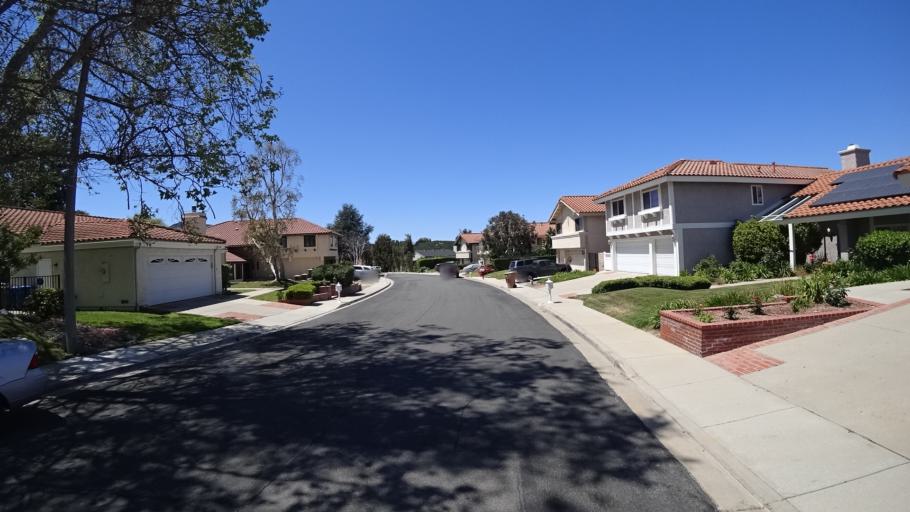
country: US
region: California
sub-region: Ventura County
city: Casa Conejo
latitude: 34.1834
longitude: -118.8952
